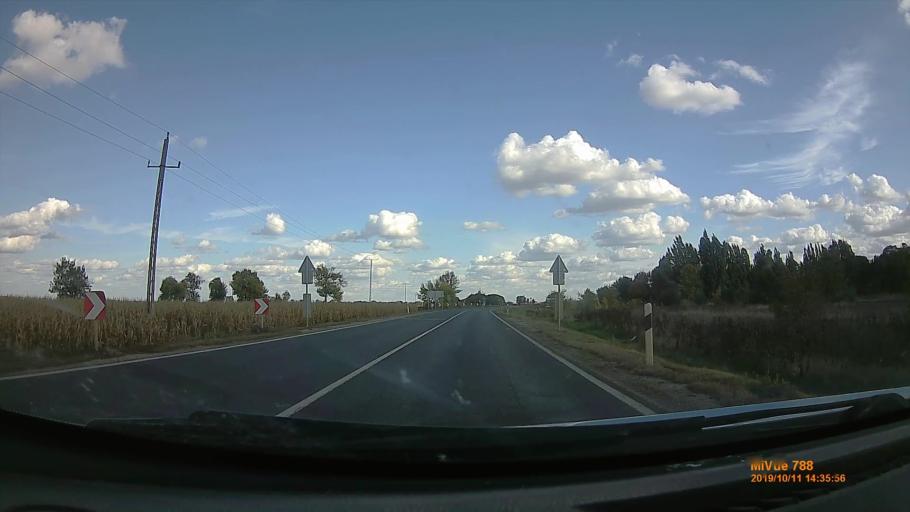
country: HU
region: Hajdu-Bihar
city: Ebes
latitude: 47.5588
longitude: 21.5005
